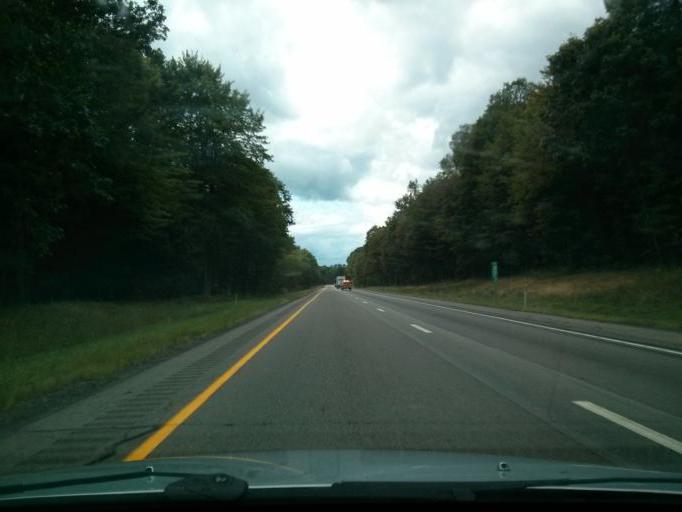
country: US
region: Pennsylvania
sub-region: Jefferson County
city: Reynoldsville
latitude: 41.1423
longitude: -78.9563
